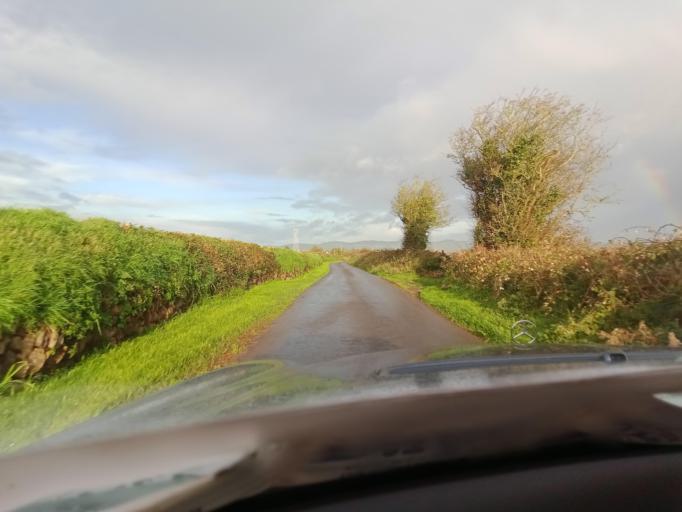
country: IE
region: Leinster
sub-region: Kilkenny
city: Mooncoin
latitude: 52.2752
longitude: -7.1907
